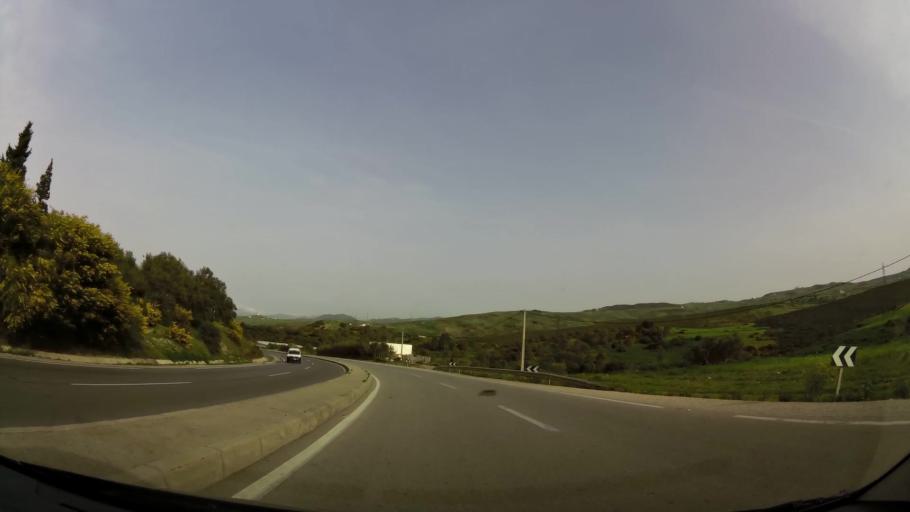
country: MA
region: Tanger-Tetouan
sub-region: Tetouan
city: Saddina
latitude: 35.5487
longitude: -5.5417
